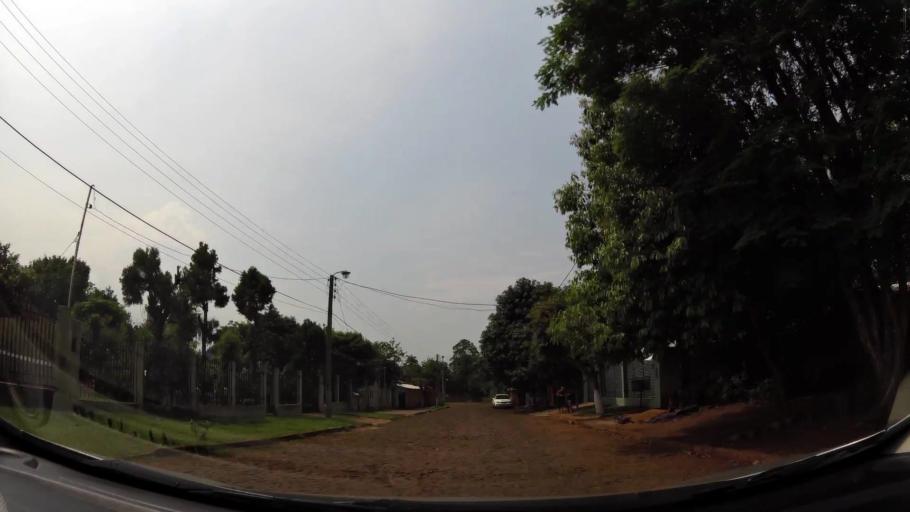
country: PY
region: Alto Parana
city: Presidente Franco
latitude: -25.5583
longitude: -54.6170
